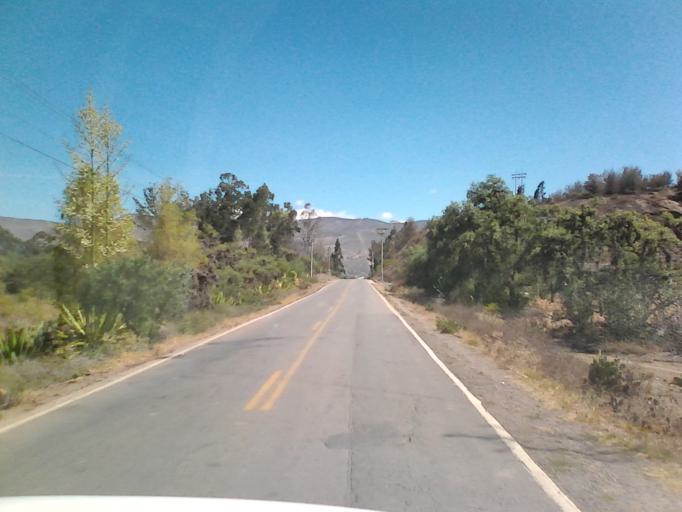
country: CO
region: Boyaca
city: Sachica
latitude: 5.5978
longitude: -73.5507
